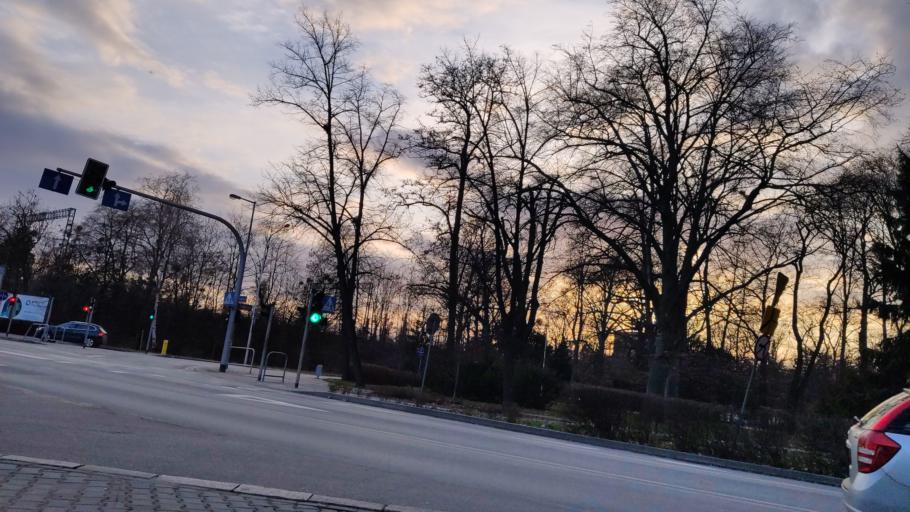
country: PL
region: Lower Silesian Voivodeship
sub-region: Powiat wroclawski
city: Wroclaw
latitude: 51.0726
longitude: 17.0121
